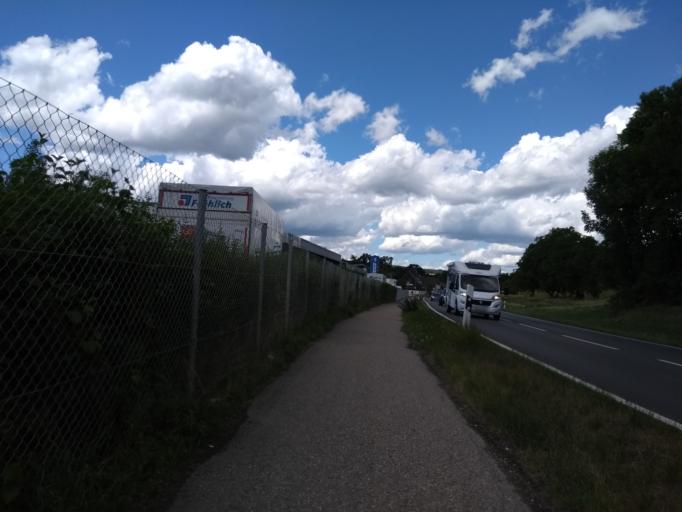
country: DE
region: Baden-Wuerttemberg
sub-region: Tuebingen Region
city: Ehingen
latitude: 48.2760
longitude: 9.7195
